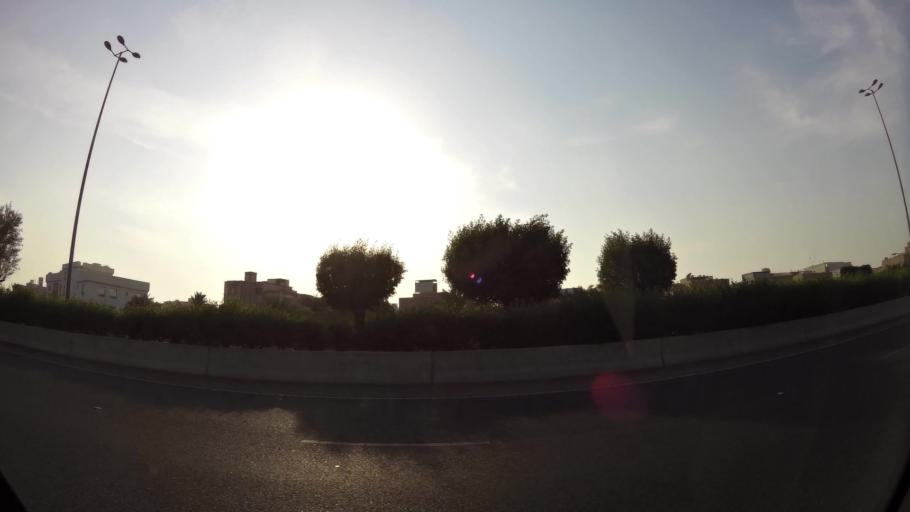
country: KW
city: Al Funaytis
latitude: 29.2159
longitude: 48.0888
